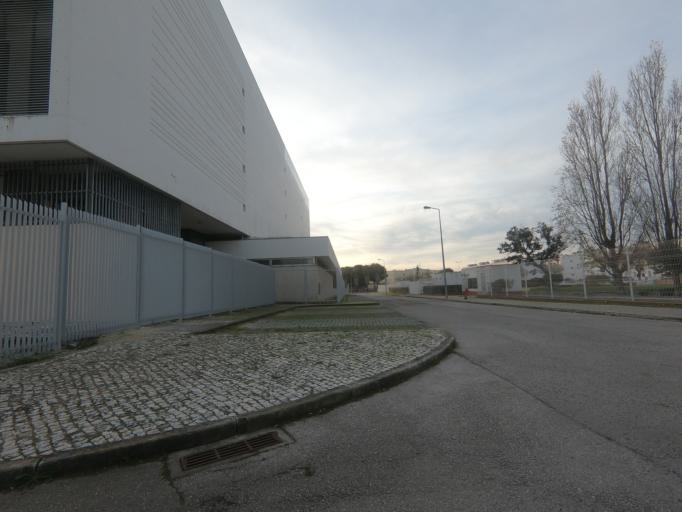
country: PT
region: Setubal
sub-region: Setubal
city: Setubal
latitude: 38.5202
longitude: -8.8472
